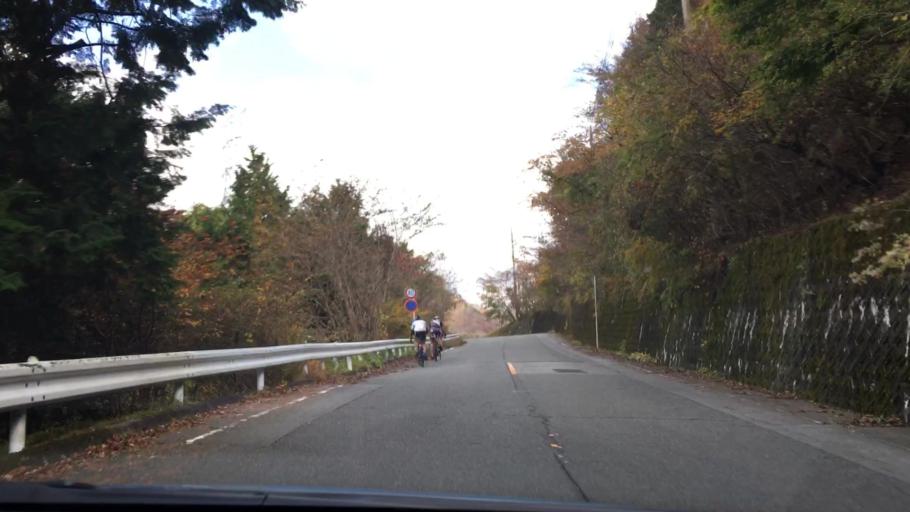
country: JP
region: Shizuoka
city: Gotemba
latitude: 35.3916
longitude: 138.9426
